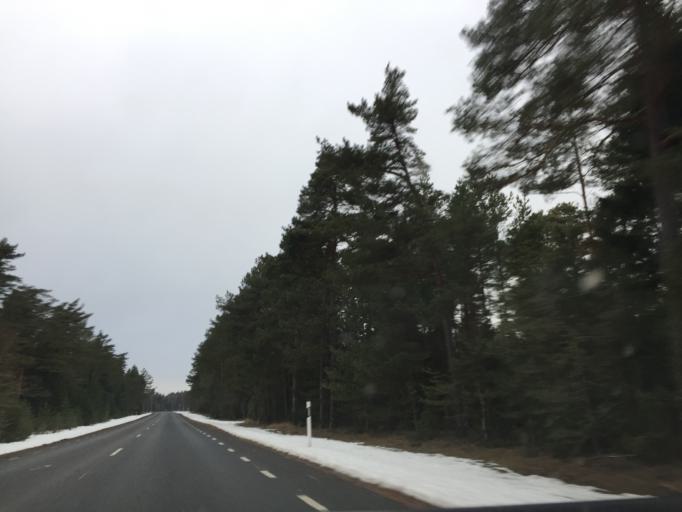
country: EE
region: Saare
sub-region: Kuressaare linn
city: Kuressaare
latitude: 58.5500
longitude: 22.3304
